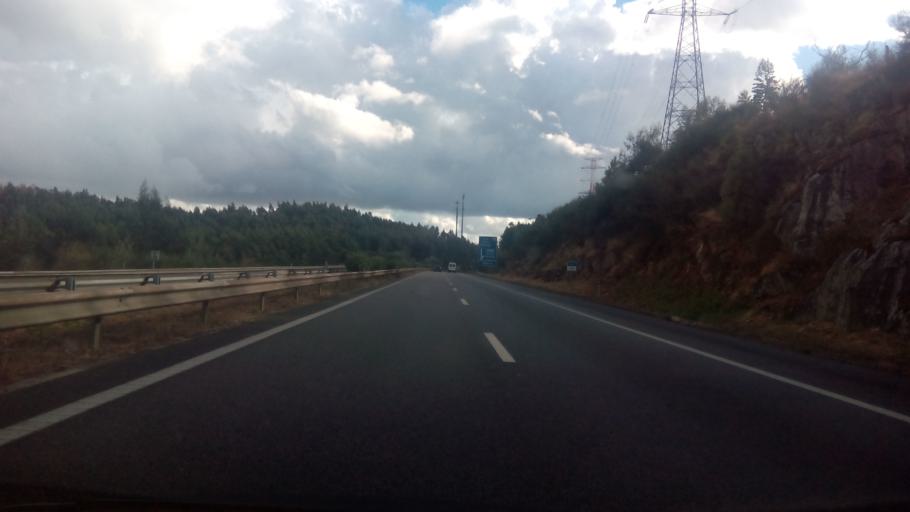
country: PT
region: Porto
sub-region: Paredes
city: Baltar
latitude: 41.1770
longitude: -8.3780
